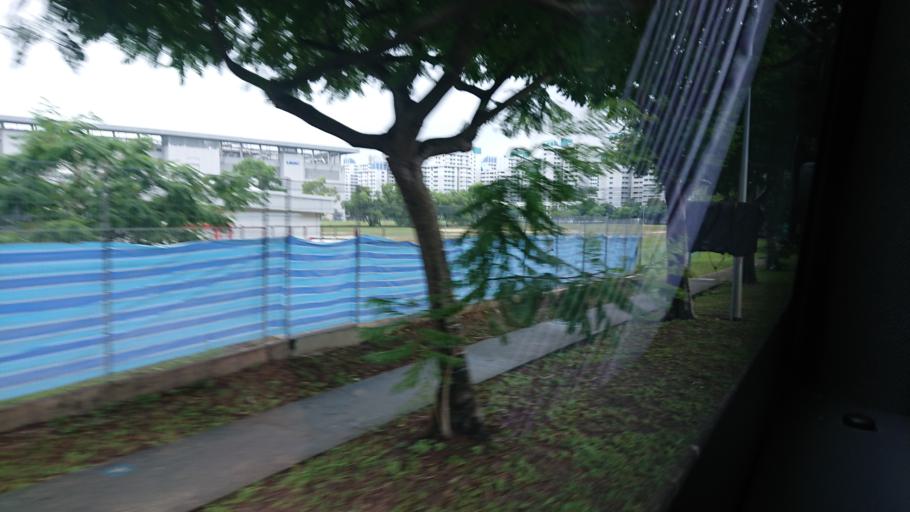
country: MY
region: Johor
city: Kampung Pasir Gudang Baru
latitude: 1.3771
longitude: 103.9300
